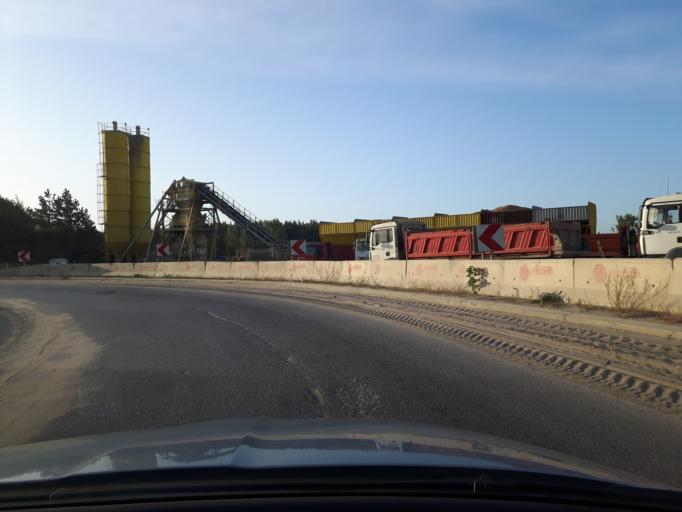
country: PL
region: Masovian Voivodeship
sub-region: Powiat piaseczynski
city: Gora Kalwaria
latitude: 51.9695
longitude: 21.2094
